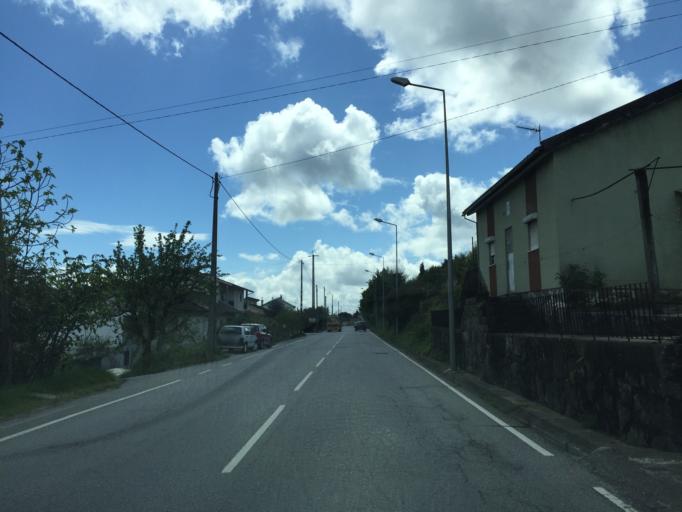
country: PT
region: Viseu
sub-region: Viseu
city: Viseu
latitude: 40.6531
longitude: -7.9467
